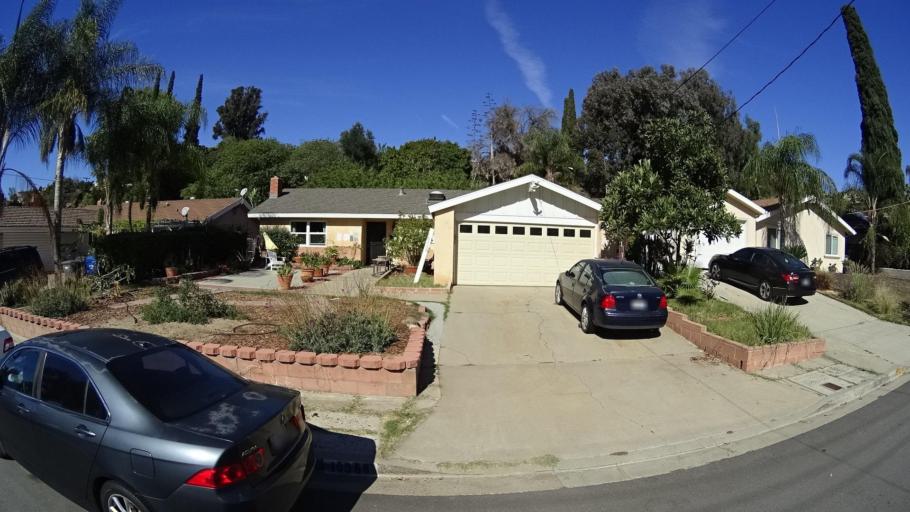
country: US
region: California
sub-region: San Diego County
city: La Presa
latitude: 32.7185
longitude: -116.9753
